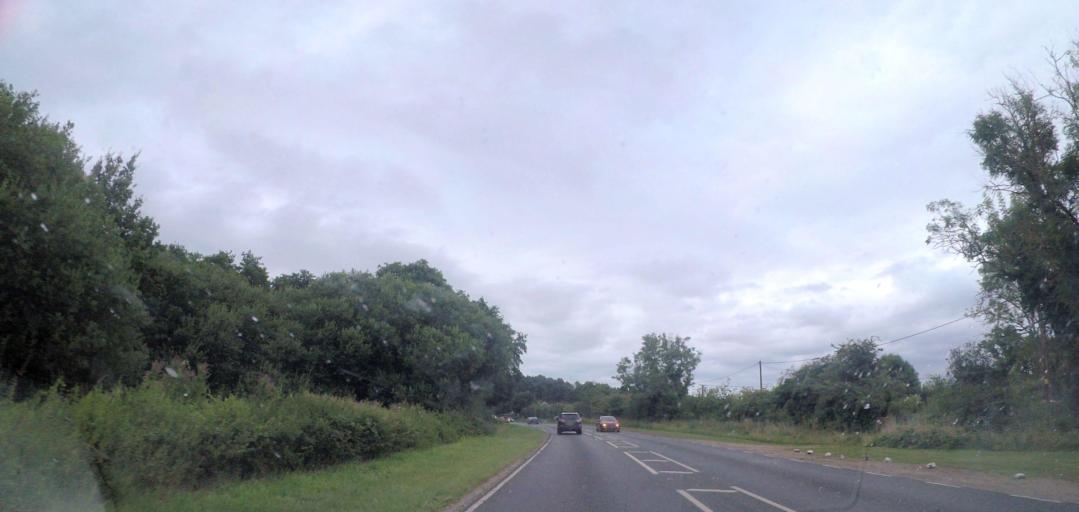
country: GB
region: England
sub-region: Norfolk
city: Spixworth
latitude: 52.6983
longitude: 1.3410
